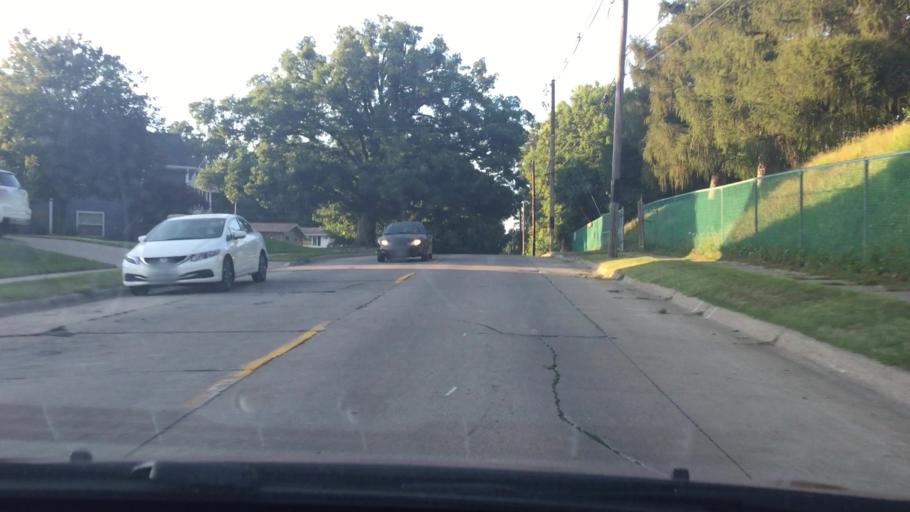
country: US
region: Iowa
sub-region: Muscatine County
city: Muscatine
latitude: 41.4253
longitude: -91.0649
